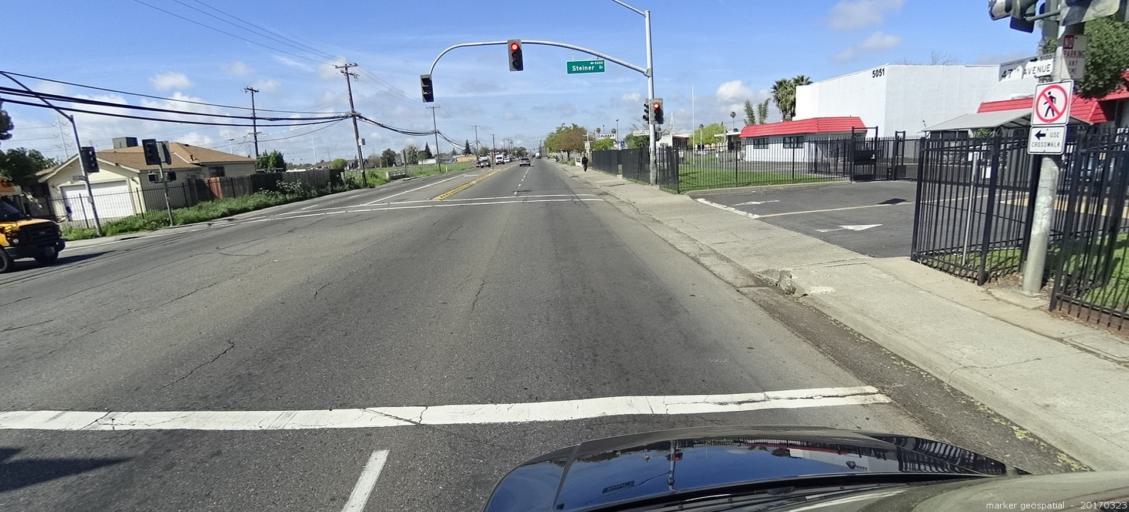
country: US
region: California
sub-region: Sacramento County
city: Parkway
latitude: 38.5105
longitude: -121.4454
